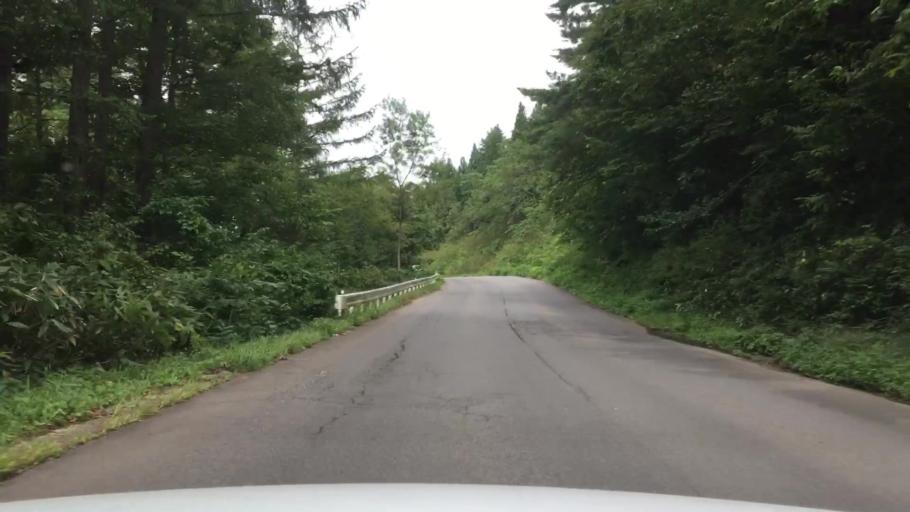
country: JP
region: Aomori
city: Shimokizukuri
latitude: 40.7187
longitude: 140.2591
